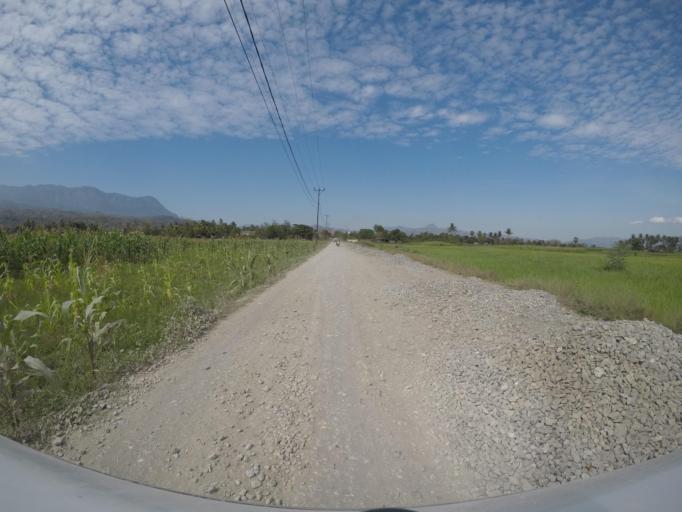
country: TL
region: Bobonaro
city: Maliana
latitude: -8.9849
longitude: 125.2107
